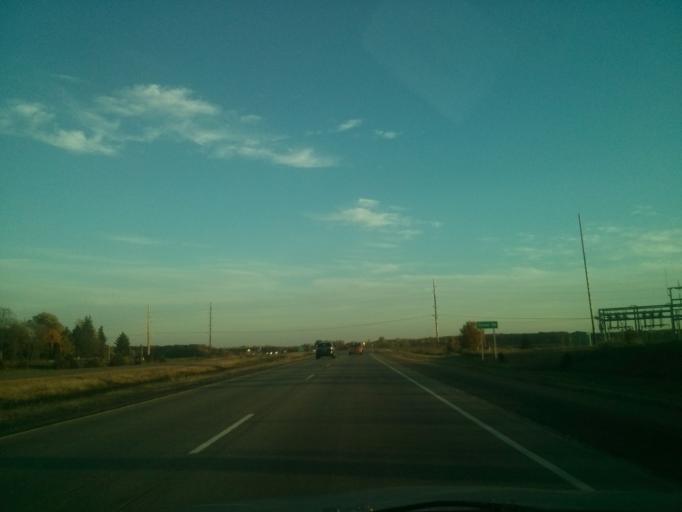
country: US
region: Wisconsin
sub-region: Pierce County
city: River Falls
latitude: 44.9150
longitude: -92.6683
